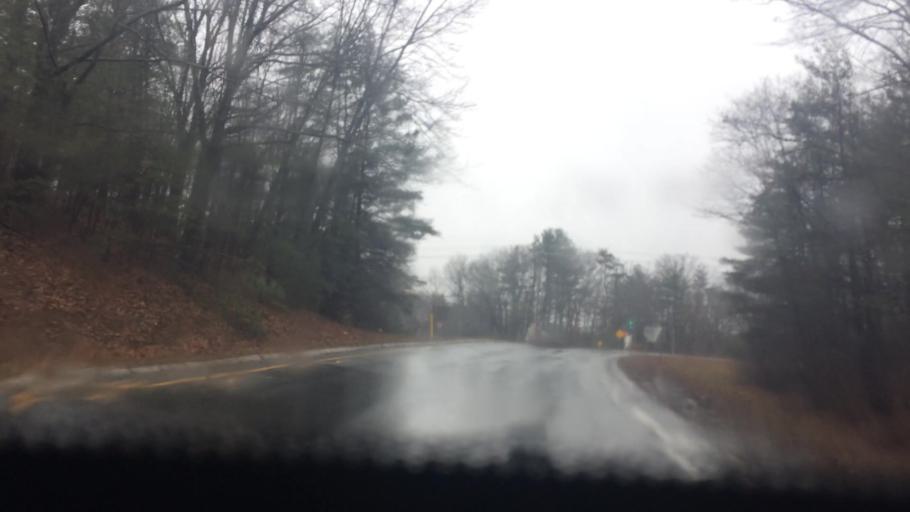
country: US
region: Massachusetts
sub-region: Essex County
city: Haverhill
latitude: 42.7614
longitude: -71.1244
